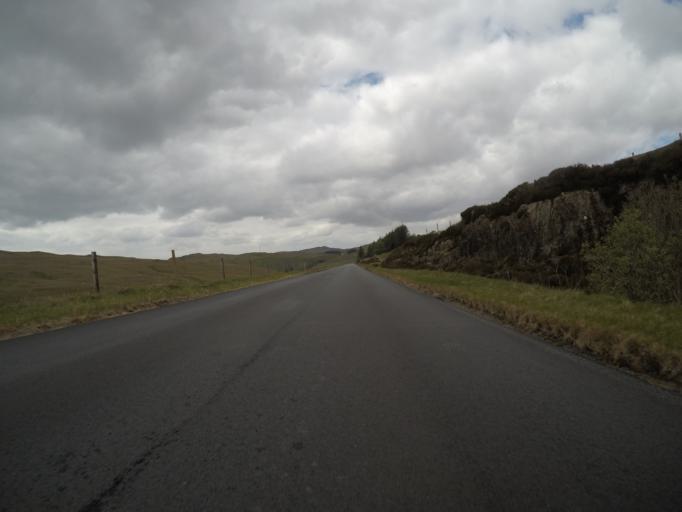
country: GB
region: Scotland
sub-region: Highland
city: Isle of Skye
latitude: 57.3223
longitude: -6.3286
